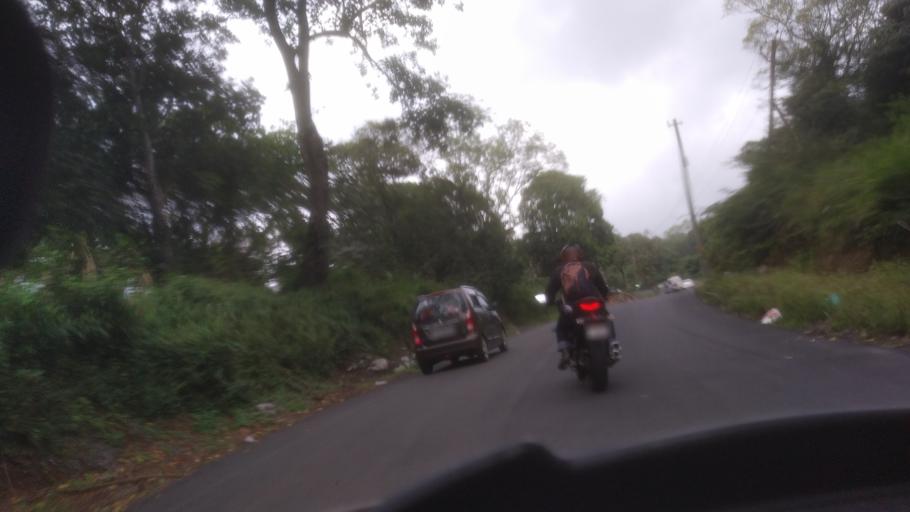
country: IN
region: Tamil Nadu
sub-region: Theni
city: Kombai
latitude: 9.8911
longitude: 77.1491
